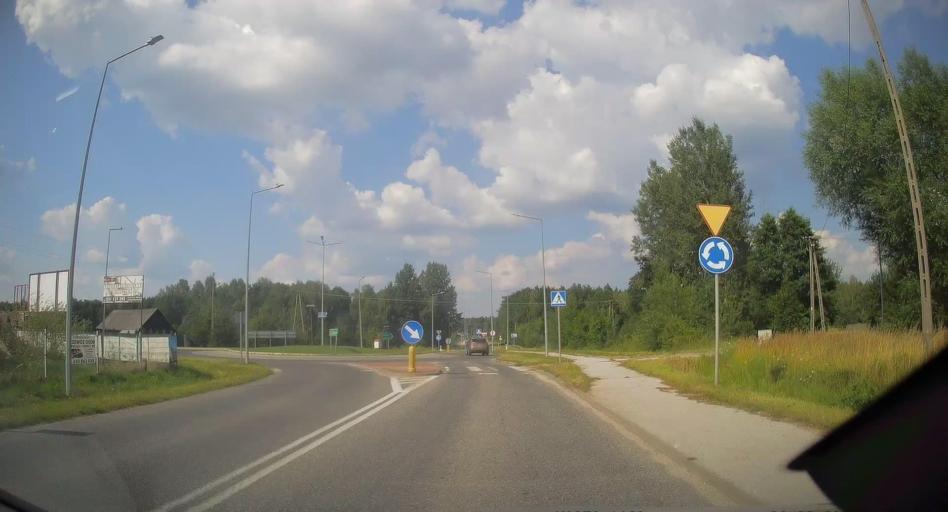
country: PL
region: Swietokrzyskie
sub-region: Powiat kielecki
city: Lopuszno
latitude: 50.9335
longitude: 20.2401
